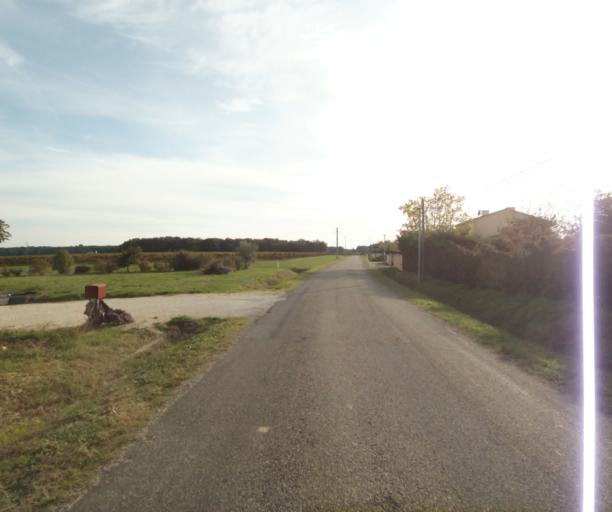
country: FR
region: Midi-Pyrenees
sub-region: Departement du Tarn-et-Garonne
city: Campsas
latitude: 43.8853
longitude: 1.3249
